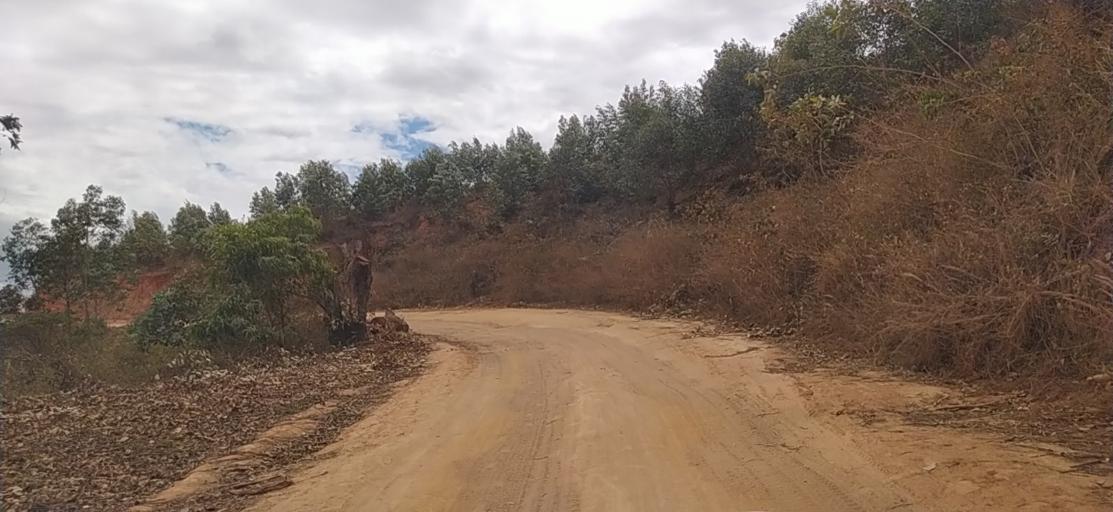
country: MG
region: Alaotra Mangoro
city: Ambatondrazaka
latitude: -18.0001
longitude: 48.2634
